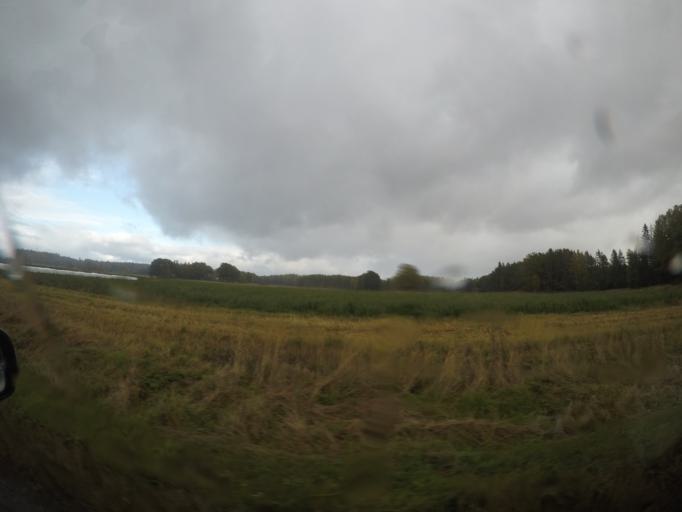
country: SE
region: Soedermanland
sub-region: Eskilstuna Kommun
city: Kvicksund
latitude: 59.3369
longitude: 16.3002
